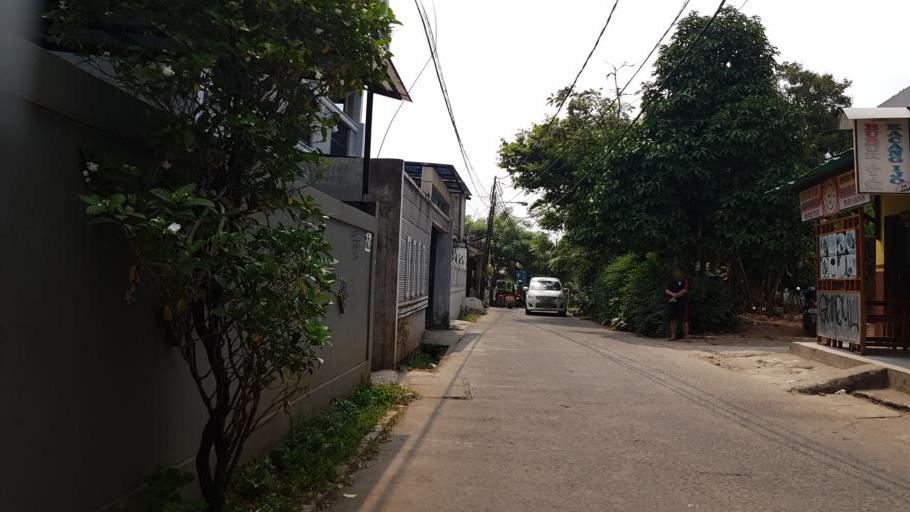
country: ID
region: West Java
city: Pamulang
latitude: -6.3304
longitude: 106.7928
